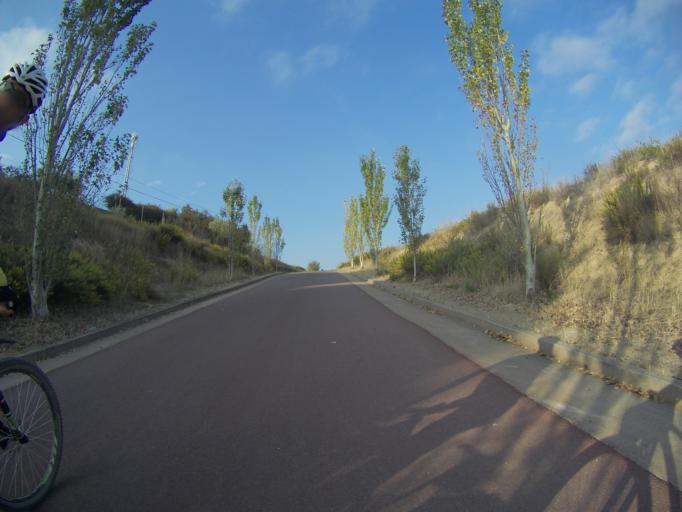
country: ES
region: Basque Country
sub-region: Provincia de Alava
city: Oyon
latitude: 42.4863
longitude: -2.4268
